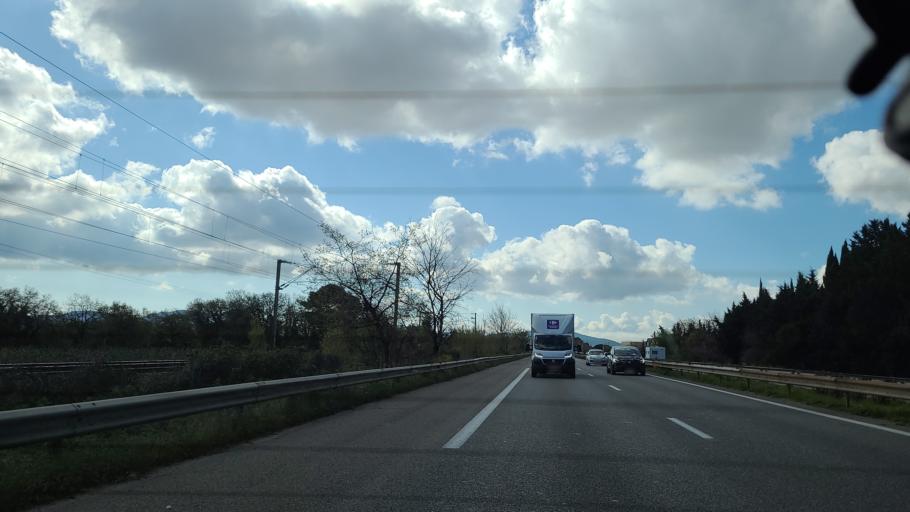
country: FR
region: Provence-Alpes-Cote d'Azur
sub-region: Departement du Var
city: La Farlede
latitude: 43.1767
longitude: 6.0483
